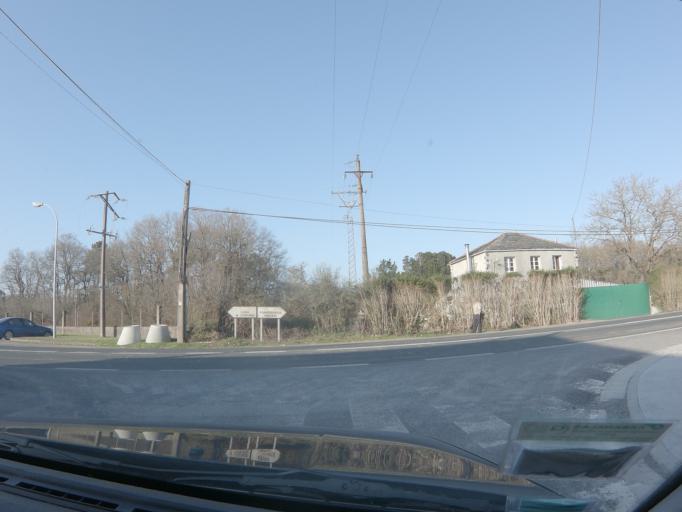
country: ES
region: Galicia
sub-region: Provincia de Lugo
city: Corgo
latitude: 42.9443
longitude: -7.4353
